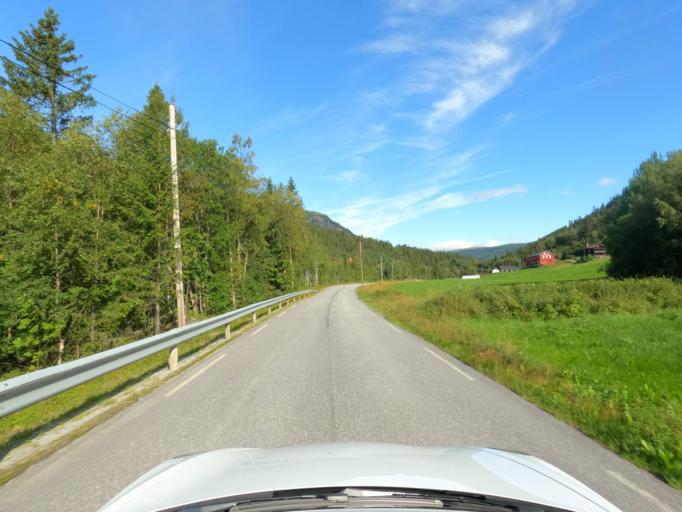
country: NO
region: Buskerud
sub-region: Nore og Uvdal
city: Rodberg
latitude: 60.0714
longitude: 8.7730
